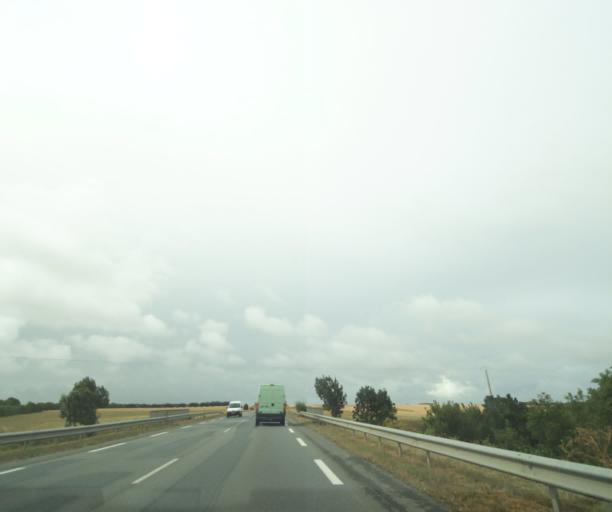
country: FR
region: Poitou-Charentes
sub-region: Departement de la Charente-Maritime
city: Lagord
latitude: 46.2054
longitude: -1.1375
